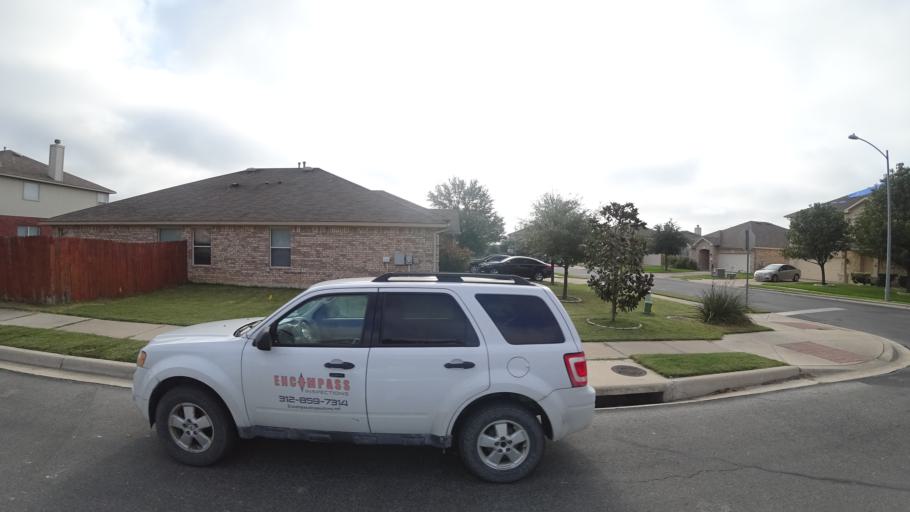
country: US
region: Texas
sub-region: Travis County
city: Pflugerville
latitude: 30.3585
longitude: -97.6412
